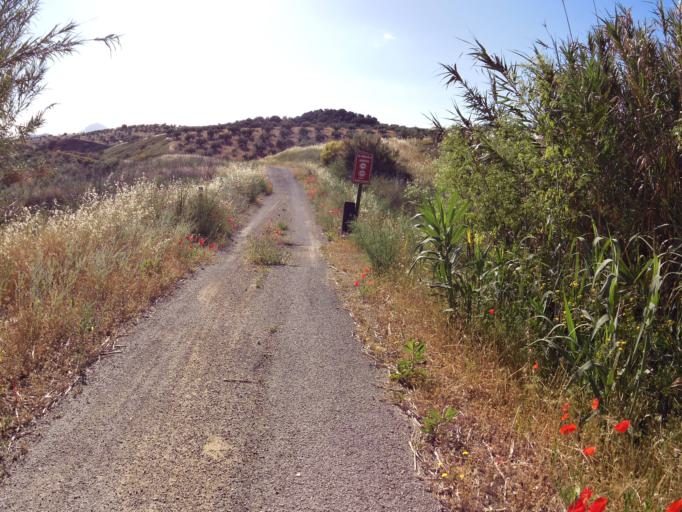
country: ES
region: Andalusia
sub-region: Province of Cordoba
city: Fuente-Tojar
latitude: 37.5787
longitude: -4.1827
